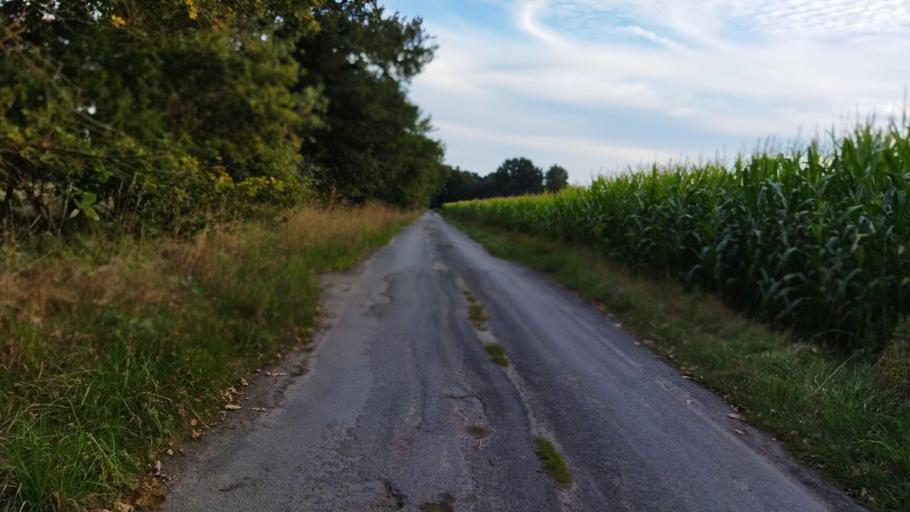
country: DE
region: Lower Saxony
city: Glandorf
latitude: 52.0944
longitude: 8.0356
